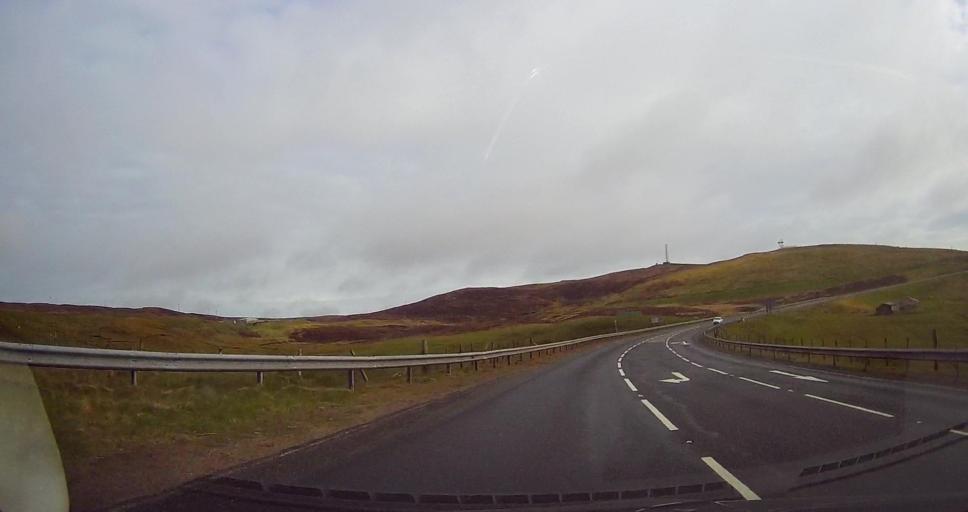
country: GB
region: Scotland
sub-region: Shetland Islands
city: Lerwick
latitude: 60.1366
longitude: -1.2138
